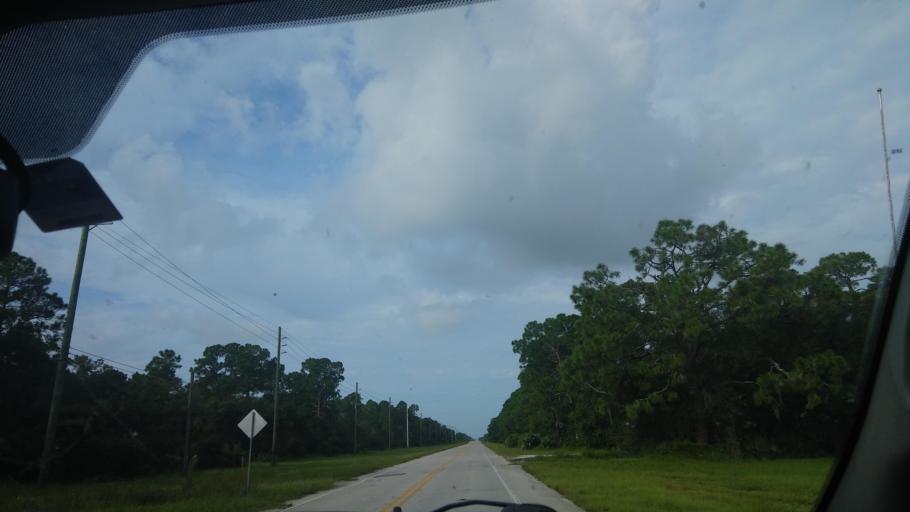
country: US
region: Florida
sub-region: Indian River County
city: Fellsmere
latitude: 27.7650
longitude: -80.6103
